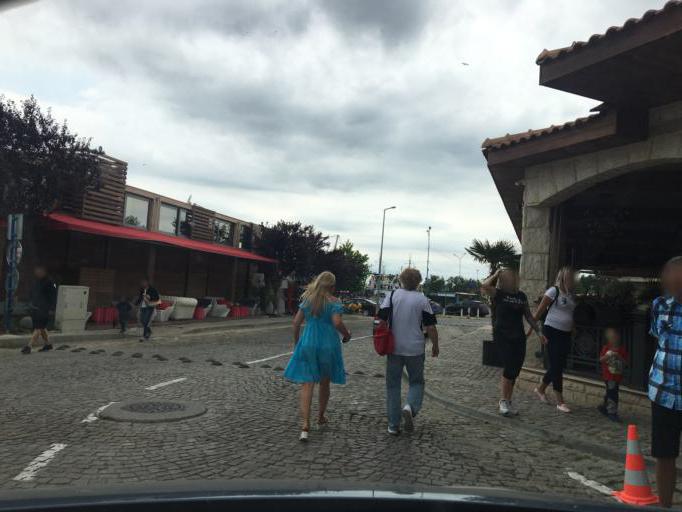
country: BG
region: Burgas
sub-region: Obshtina Sozopol
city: Sozopol
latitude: 42.4213
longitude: 27.6924
